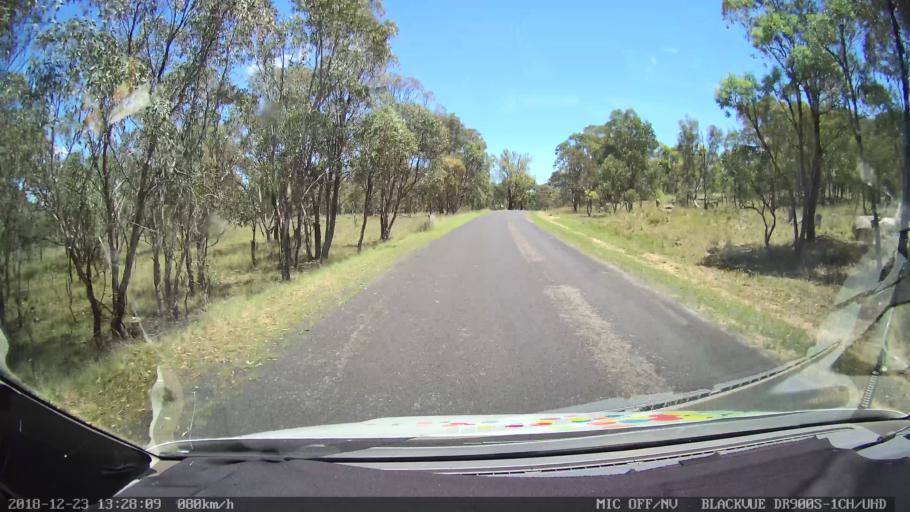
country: AU
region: New South Wales
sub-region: Armidale Dumaresq
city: Armidale
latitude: -30.4647
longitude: 151.3518
